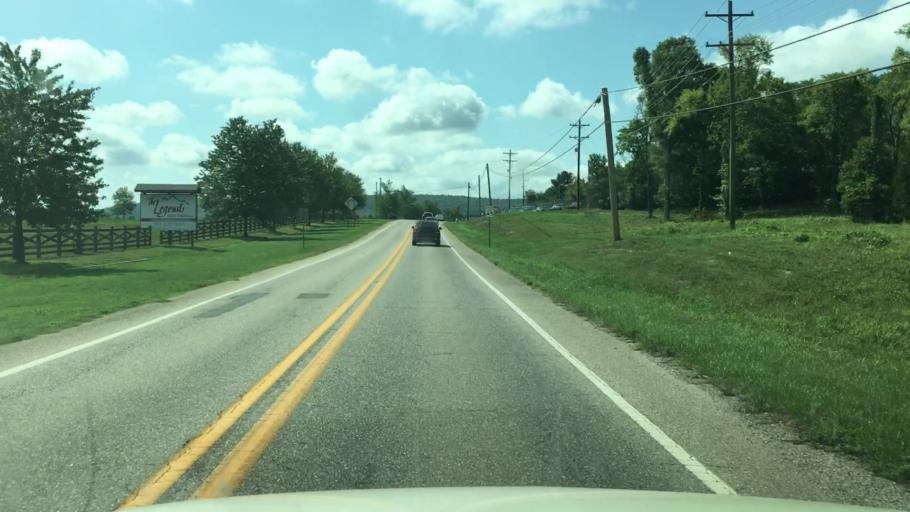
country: US
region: Arkansas
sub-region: Garland County
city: Lake Hamilton
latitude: 34.4090
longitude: -93.0924
